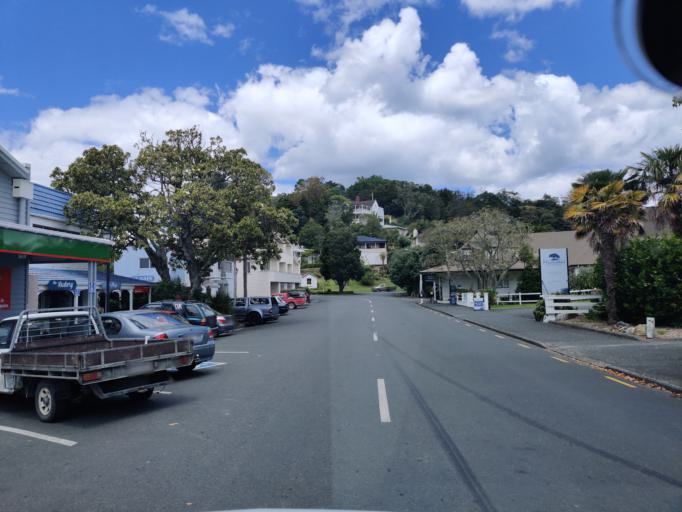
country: NZ
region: Northland
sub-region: Far North District
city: Paihia
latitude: -35.2626
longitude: 174.1225
